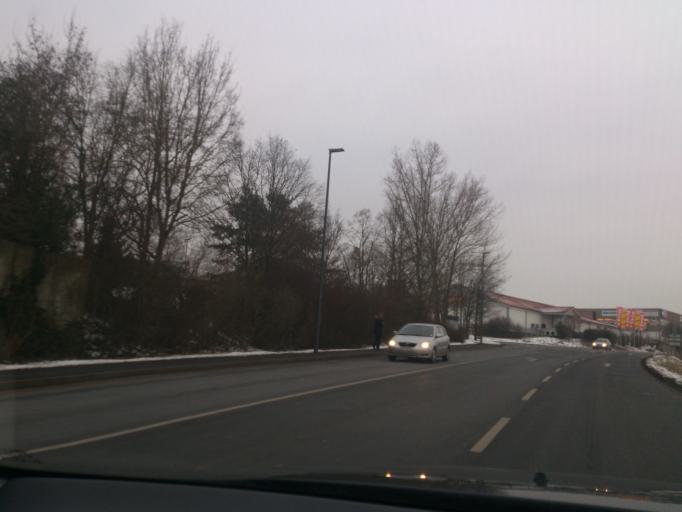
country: DE
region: Bavaria
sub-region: Regierungsbezirk Unterfranken
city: Wuerzburg
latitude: 49.7739
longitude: 9.8690
